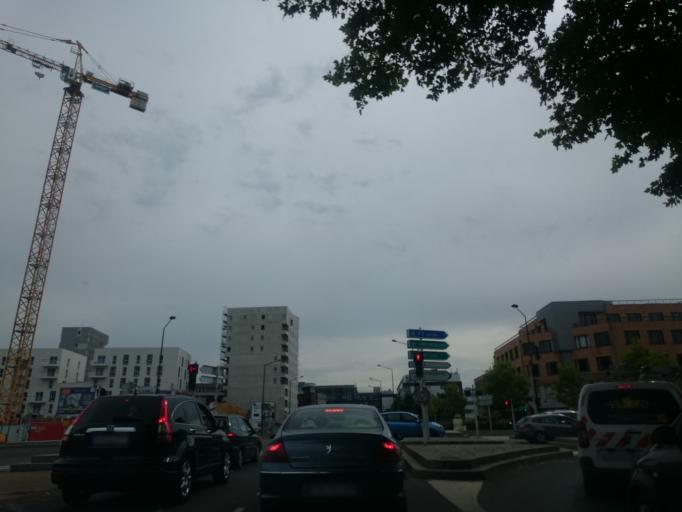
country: FR
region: Ile-de-France
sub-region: Departement de l'Essonne
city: Courcouronnes
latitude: 48.6254
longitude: 2.4237
